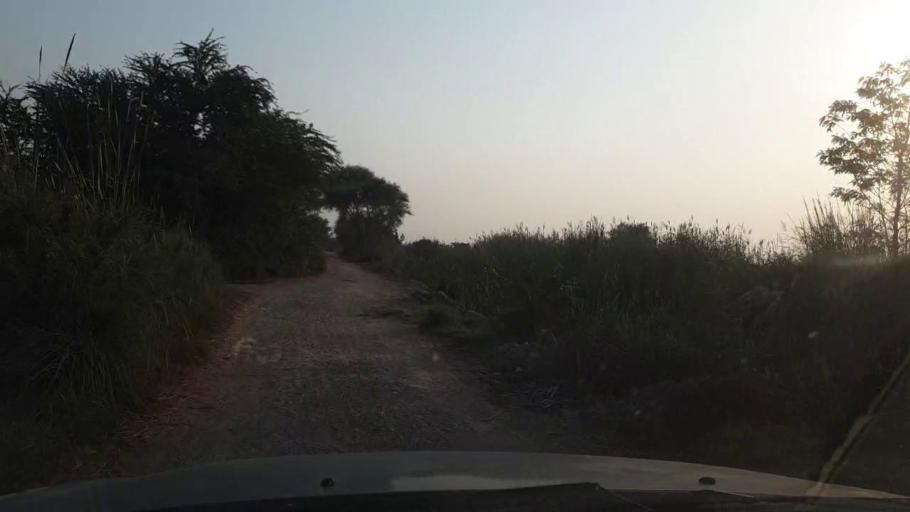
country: PK
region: Sindh
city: Tando Muhammad Khan
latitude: 25.0098
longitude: 68.4365
